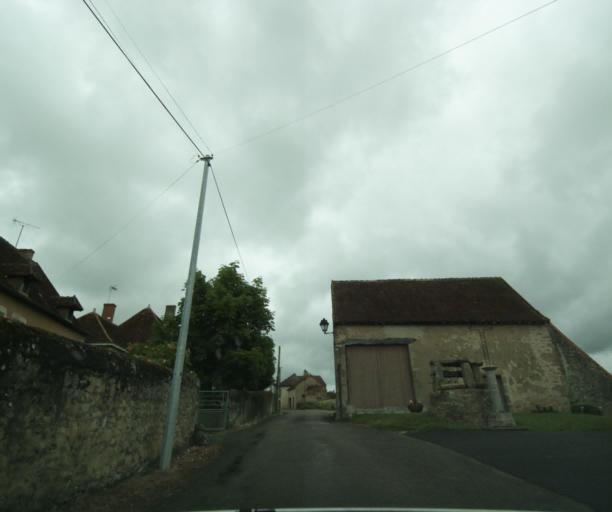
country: FR
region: Bourgogne
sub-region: Departement de Saone-et-Loire
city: Charolles
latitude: 46.4730
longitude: 4.3353
